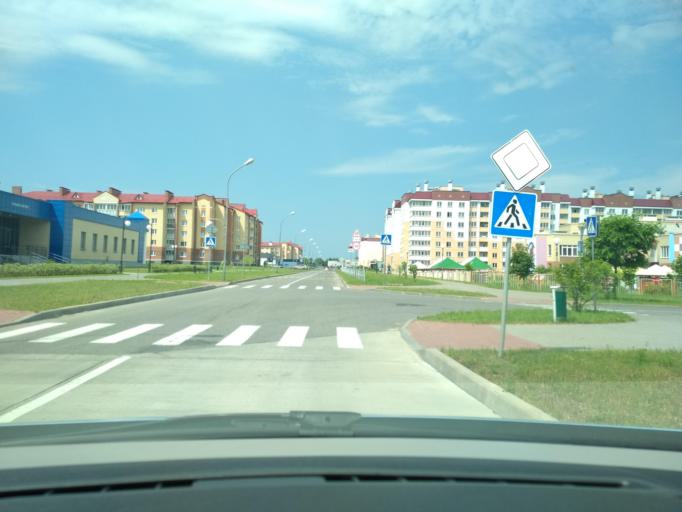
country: BY
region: Grodnenskaya
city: Astravyets
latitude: 54.6056
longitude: 25.9725
